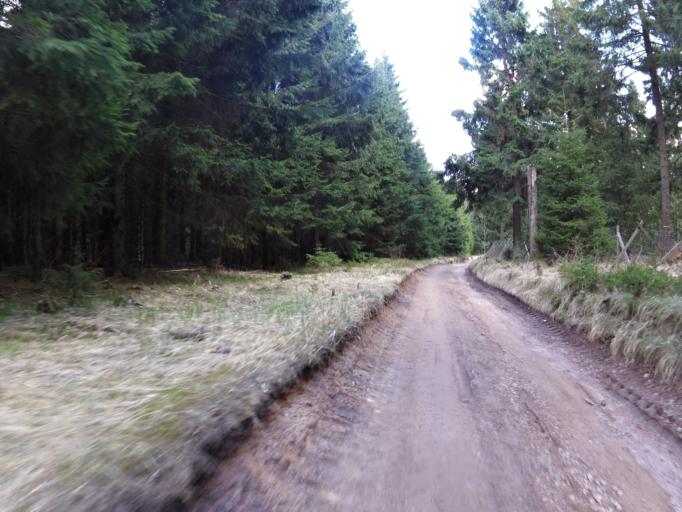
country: DE
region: Thuringia
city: Bermbach
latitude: 50.7115
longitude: 10.6612
